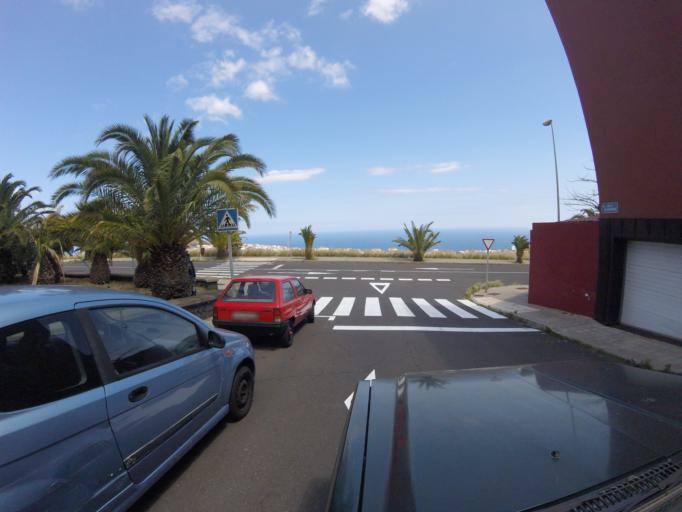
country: ES
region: Canary Islands
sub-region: Provincia de Santa Cruz de Tenerife
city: La Laguna
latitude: 28.4430
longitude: -16.3102
